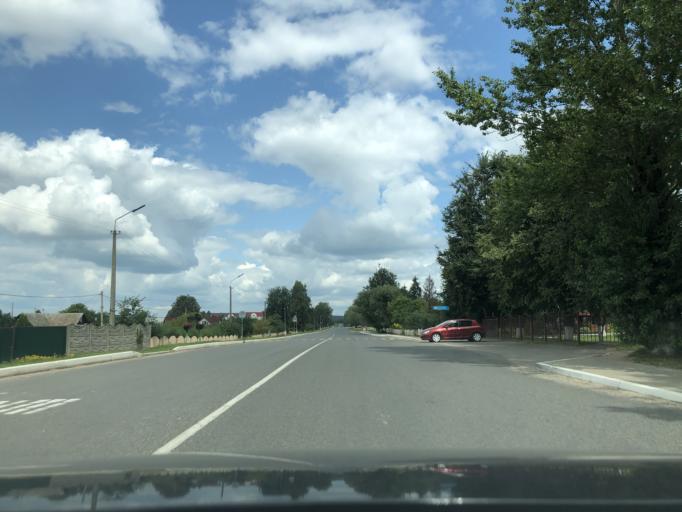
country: BY
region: Minsk
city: Lahoysk
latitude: 54.2114
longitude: 27.8518
